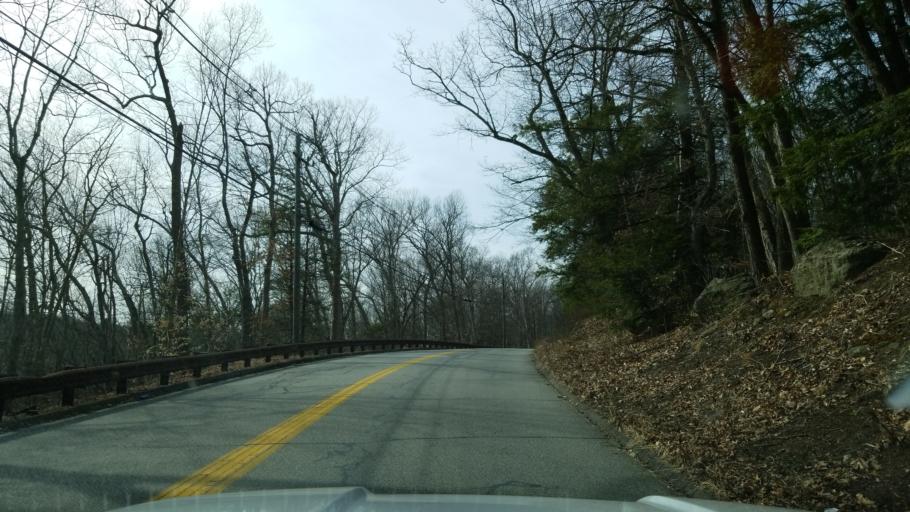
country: US
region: Connecticut
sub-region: Hartford County
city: Glastonbury Center
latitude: 41.6619
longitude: -72.5888
